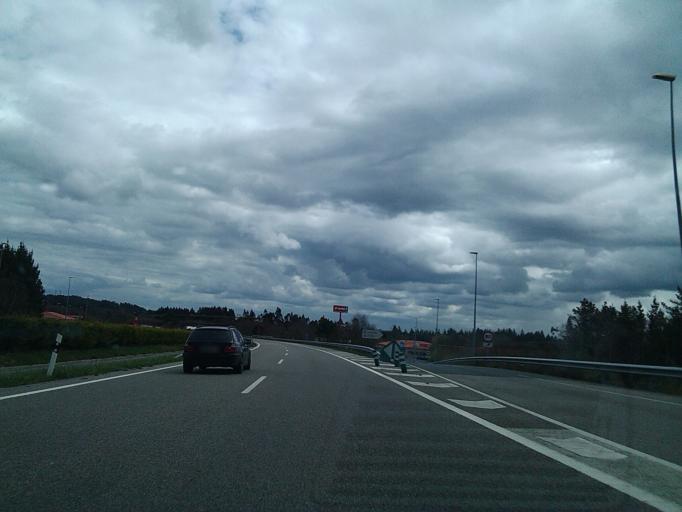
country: ES
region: Galicia
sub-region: Provincia de Lugo
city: Guitiriz
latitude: 43.1884
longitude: -7.9310
